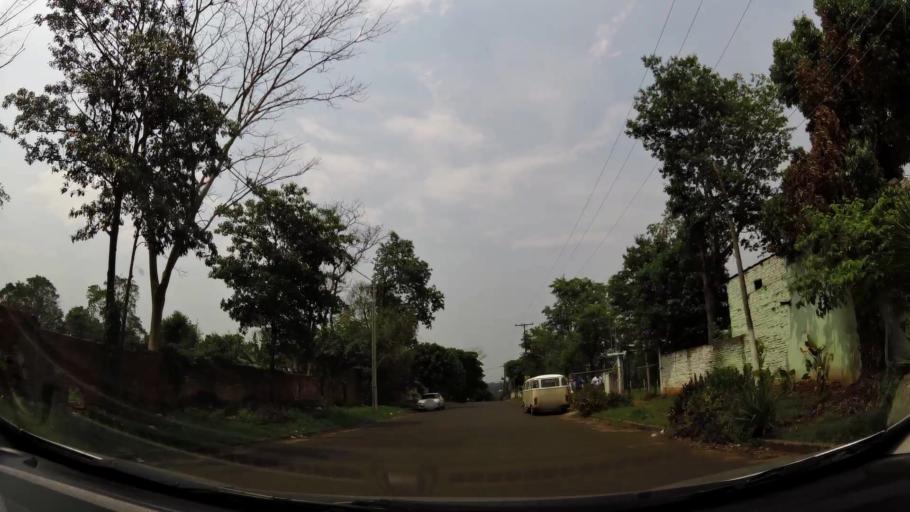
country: BR
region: Parana
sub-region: Foz Do Iguacu
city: Foz do Iguacu
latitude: -25.5636
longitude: -54.6029
